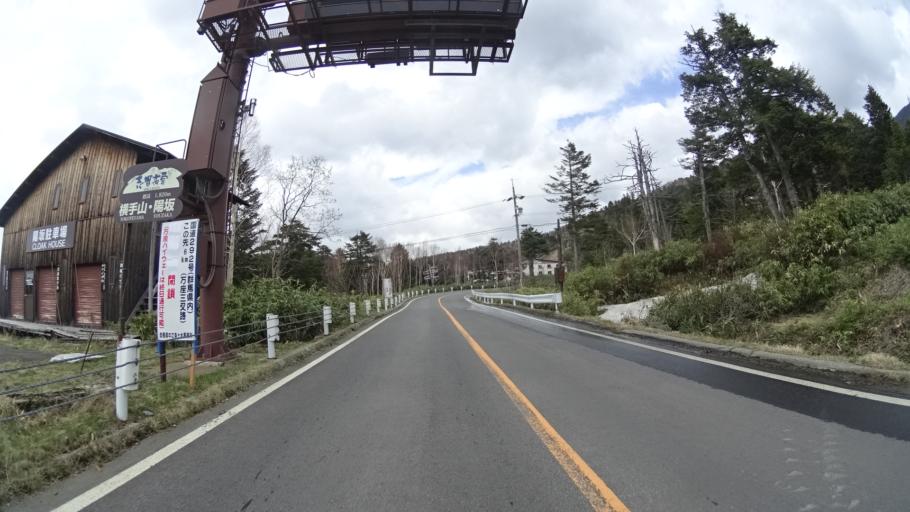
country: JP
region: Nagano
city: Nakano
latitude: 36.6764
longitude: 138.5086
